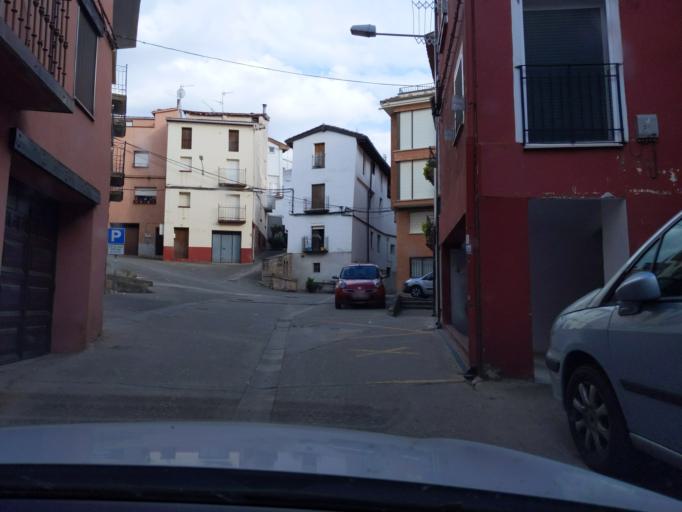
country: ES
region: La Rioja
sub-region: Provincia de La Rioja
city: Nalda
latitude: 42.3337
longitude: -2.4865
